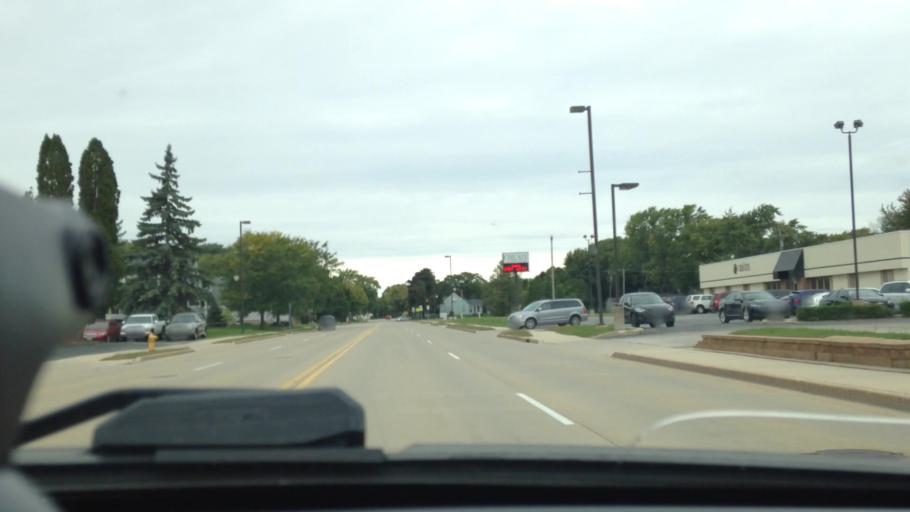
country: US
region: Wisconsin
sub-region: Fond du Lac County
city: North Fond du Lac
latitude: 43.8031
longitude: -88.4802
